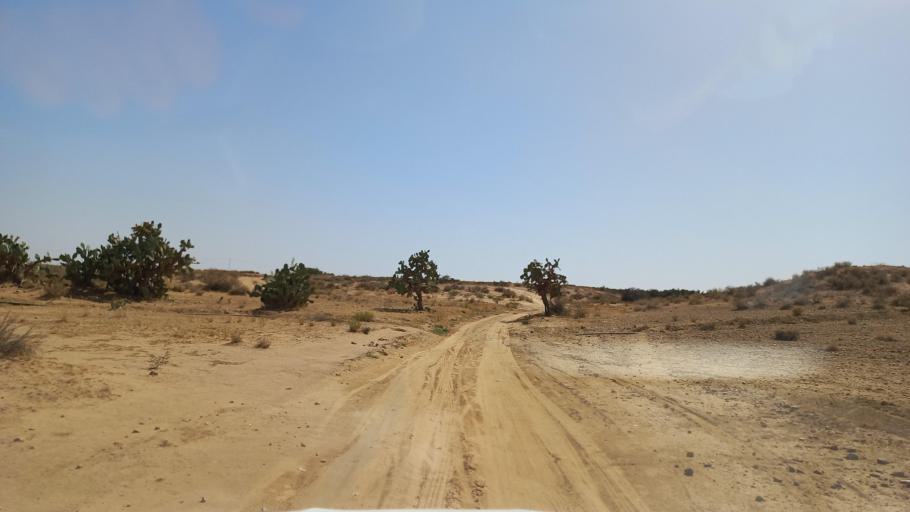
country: TN
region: Al Qasrayn
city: Kasserine
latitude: 35.2215
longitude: 9.0358
